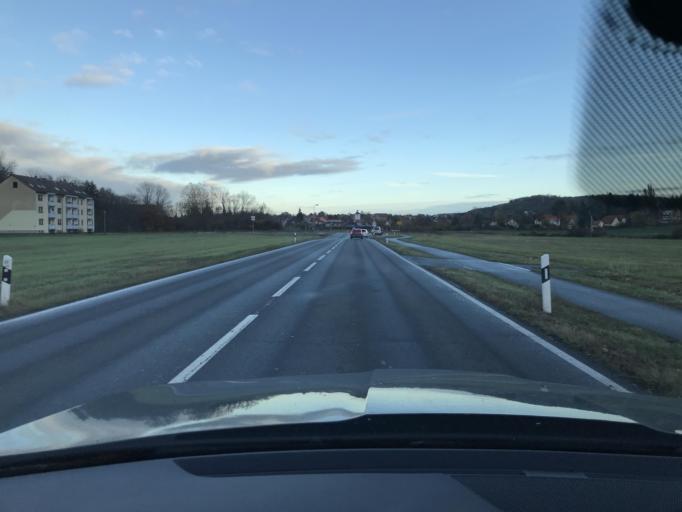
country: DE
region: Saxony-Anhalt
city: Neinstedt
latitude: 51.7513
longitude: 11.0755
